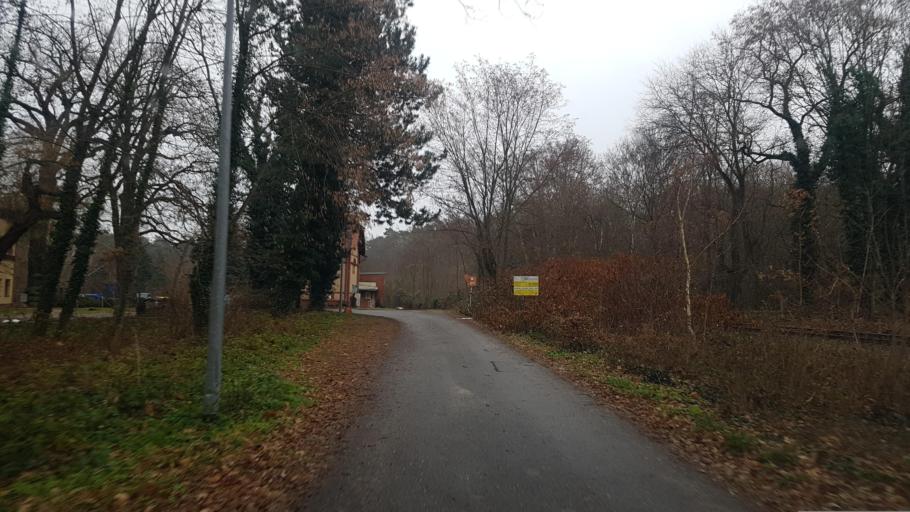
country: DE
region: Brandenburg
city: Cottbus
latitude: 51.7376
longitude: 14.3457
